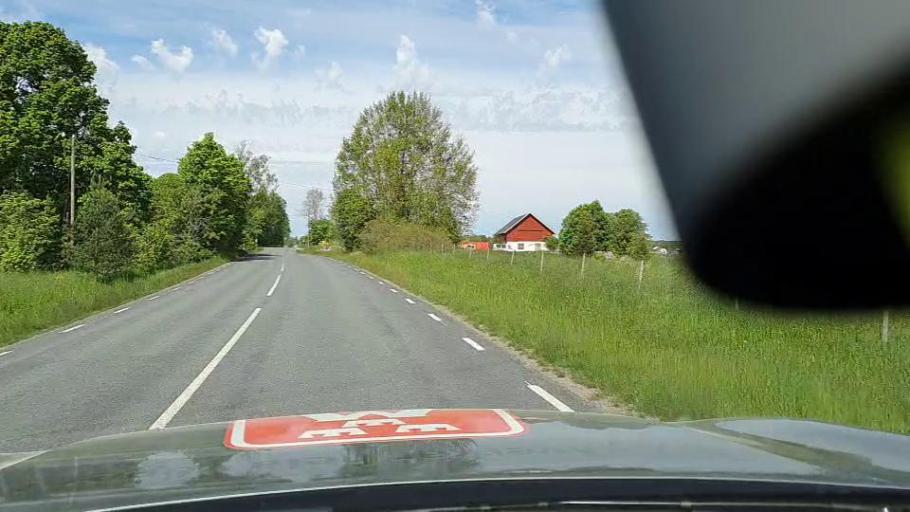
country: SE
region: Soedermanland
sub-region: Eskilstuna Kommun
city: Skogstorp
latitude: 59.3065
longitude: 16.4629
